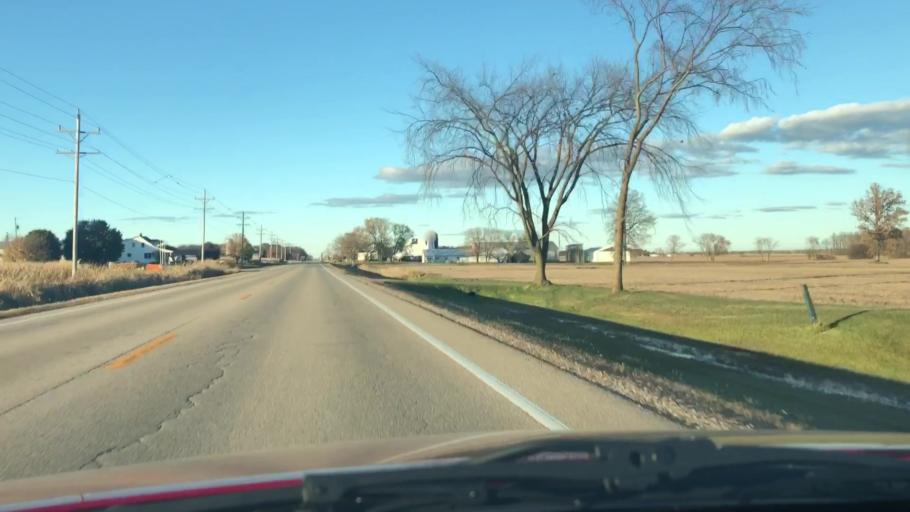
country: US
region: Wisconsin
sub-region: Outagamie County
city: Seymour
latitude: 44.4489
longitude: -88.2912
